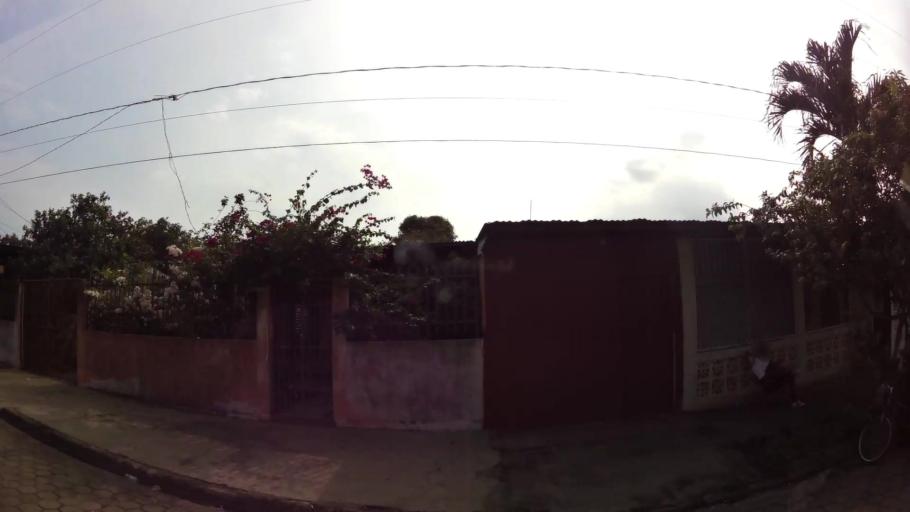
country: NI
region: Masaya
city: Masaya
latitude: 11.9674
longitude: -86.0963
